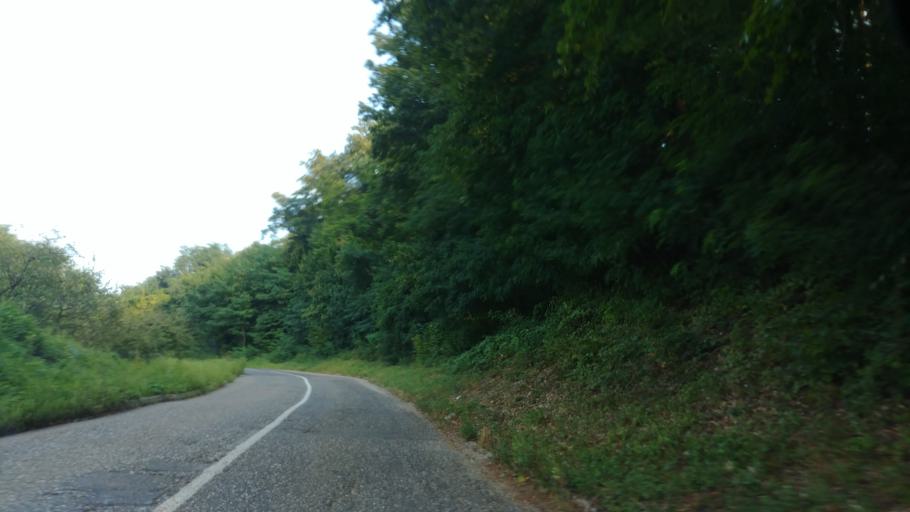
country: BA
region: Republika Srpska
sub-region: Opstina Ugljevik
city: Ugljevik
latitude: 44.7059
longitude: 18.9575
